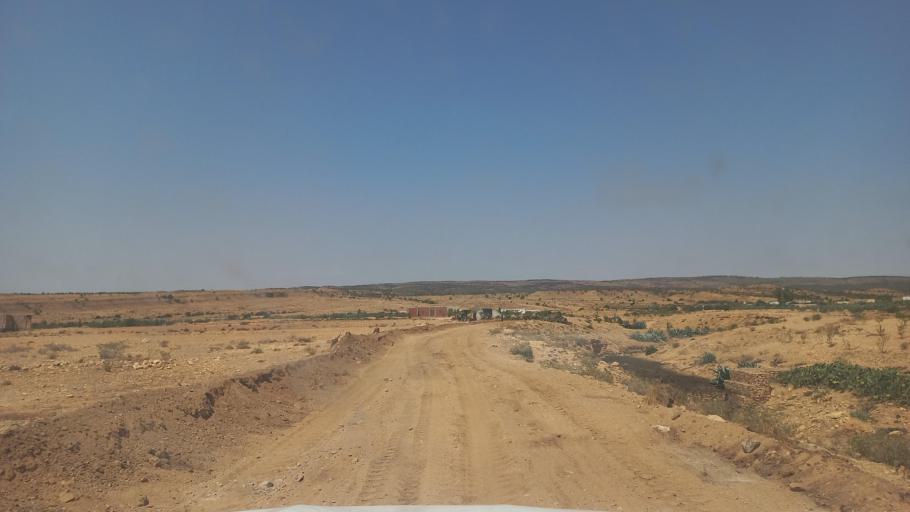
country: TN
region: Al Qasrayn
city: Kasserine
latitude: 35.2967
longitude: 8.9413
